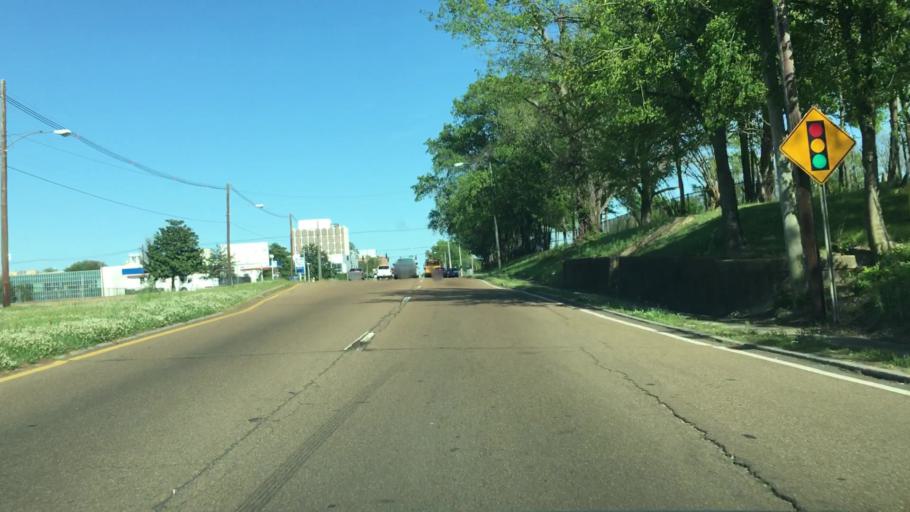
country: US
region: Mississippi
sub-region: Hinds County
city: Jackson
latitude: 32.3268
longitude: -90.1843
